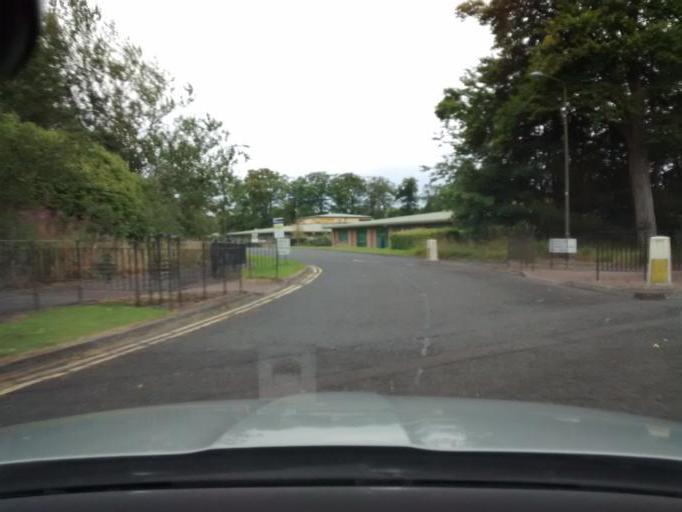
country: GB
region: Scotland
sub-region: West Lothian
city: Livingston
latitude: 55.8822
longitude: -3.5344
